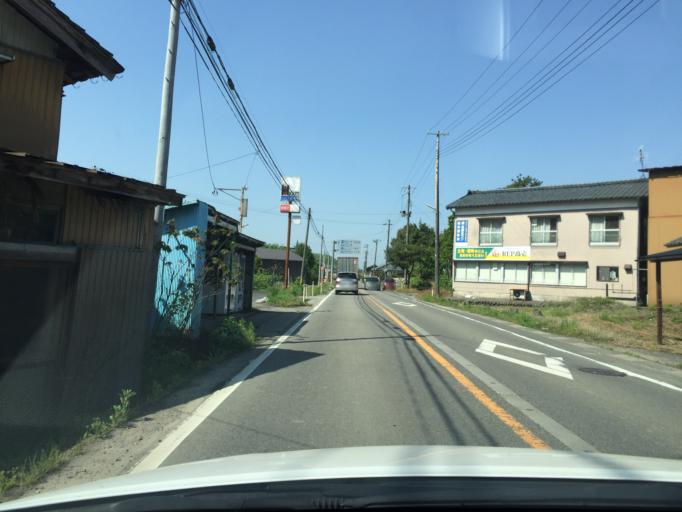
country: JP
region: Niigata
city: Muramatsu
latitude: 37.7085
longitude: 139.2041
